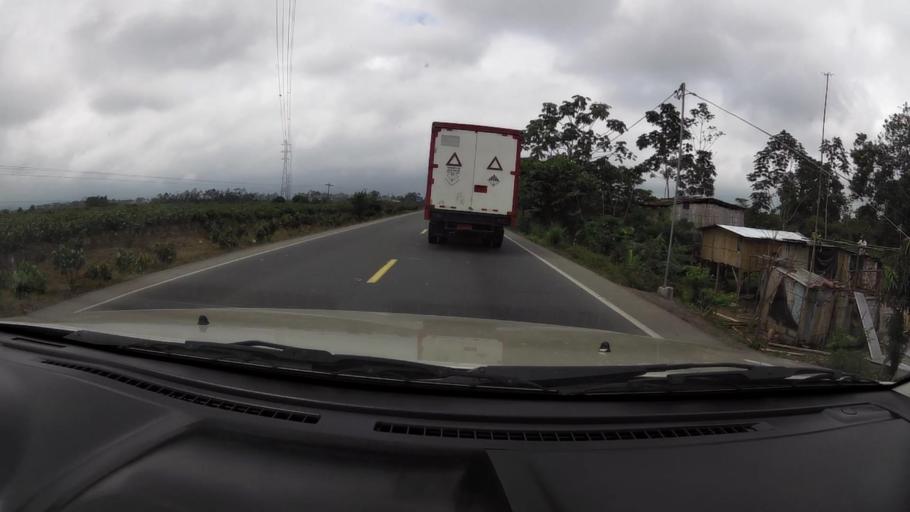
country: EC
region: Guayas
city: Balao
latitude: -2.8958
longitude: -79.7057
